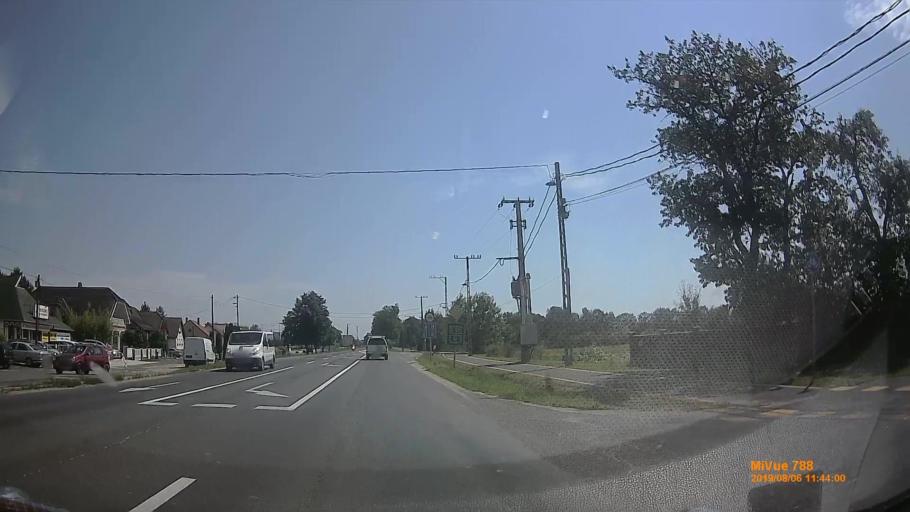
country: HU
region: Vas
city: Kormend
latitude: 47.0078
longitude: 16.5619
